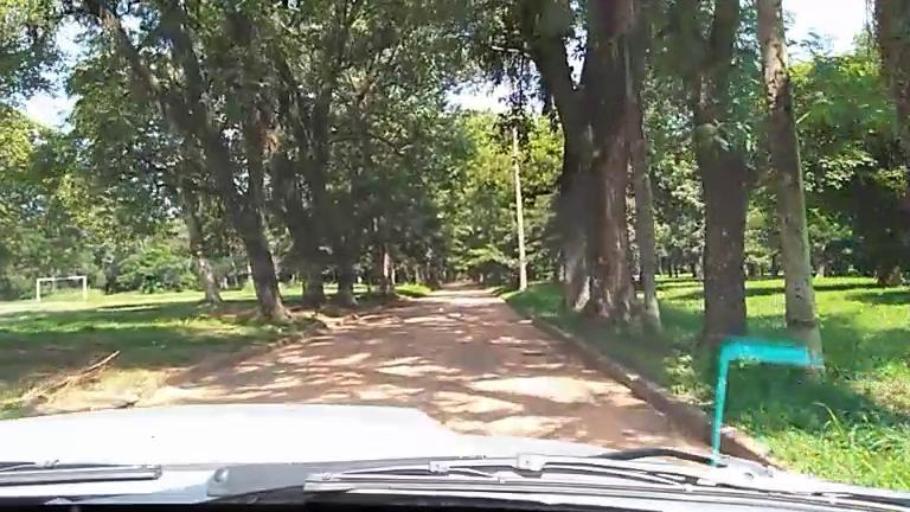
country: PY
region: Asuncion
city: Asuncion
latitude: -25.2468
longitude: -57.5768
